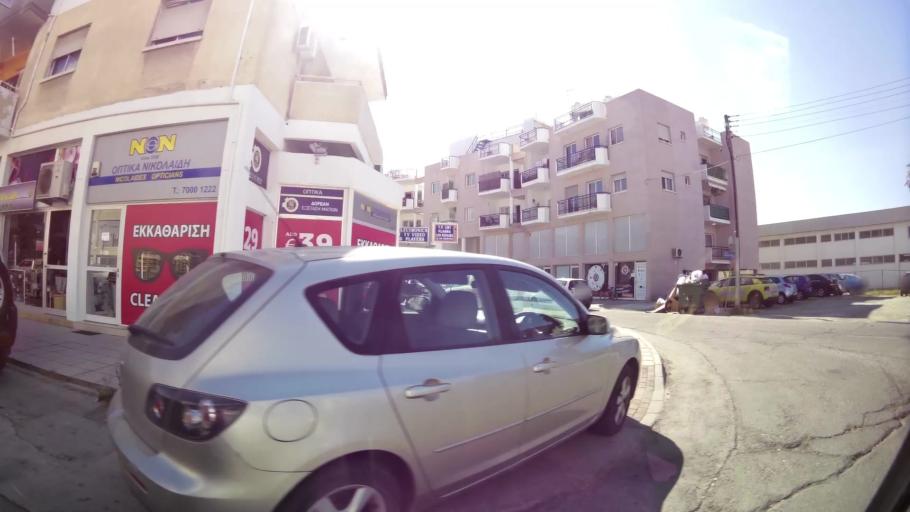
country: CY
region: Larnaka
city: Larnaca
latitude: 34.9236
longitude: 33.6345
